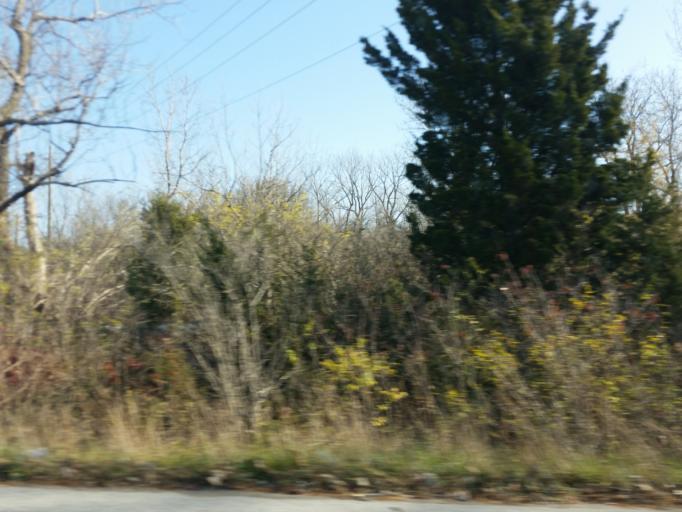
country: US
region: Indiana
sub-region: Marion County
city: Beech Grove
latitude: 39.7261
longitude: -86.0827
